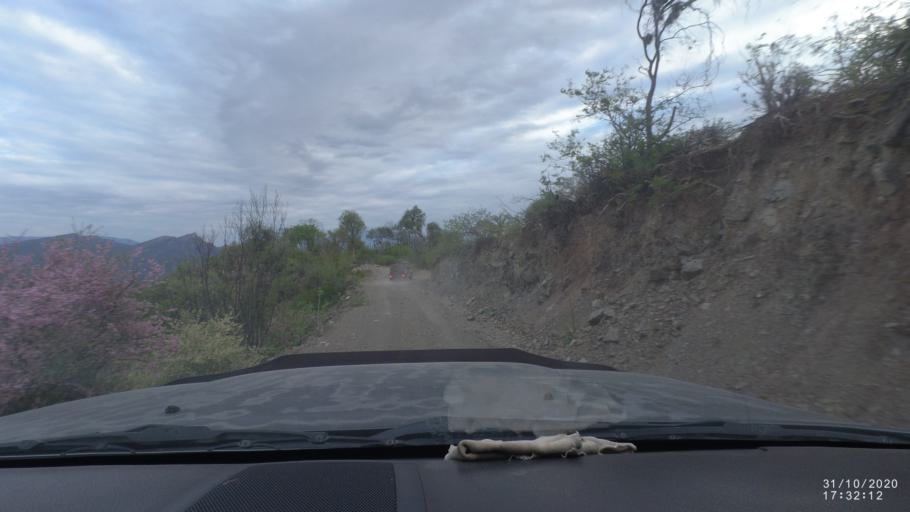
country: BO
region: Chuquisaca
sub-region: Provincia Zudanez
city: Mojocoya
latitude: -18.5978
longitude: -64.5533
